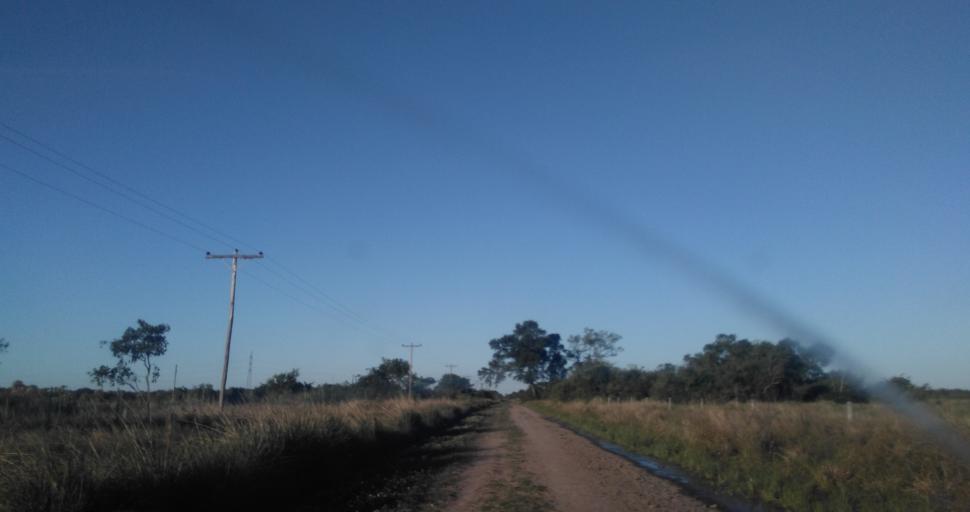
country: AR
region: Chaco
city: Fontana
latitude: -27.3923
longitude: -58.9801
